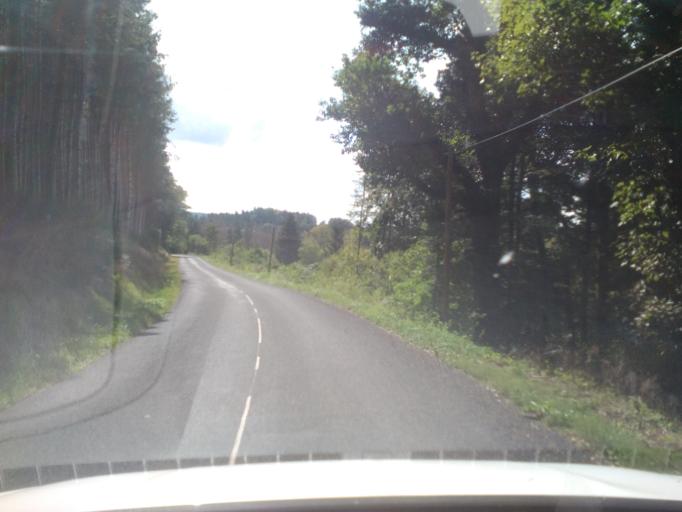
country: FR
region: Lorraine
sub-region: Departement des Vosges
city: Senones
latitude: 48.3678
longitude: 7.0294
